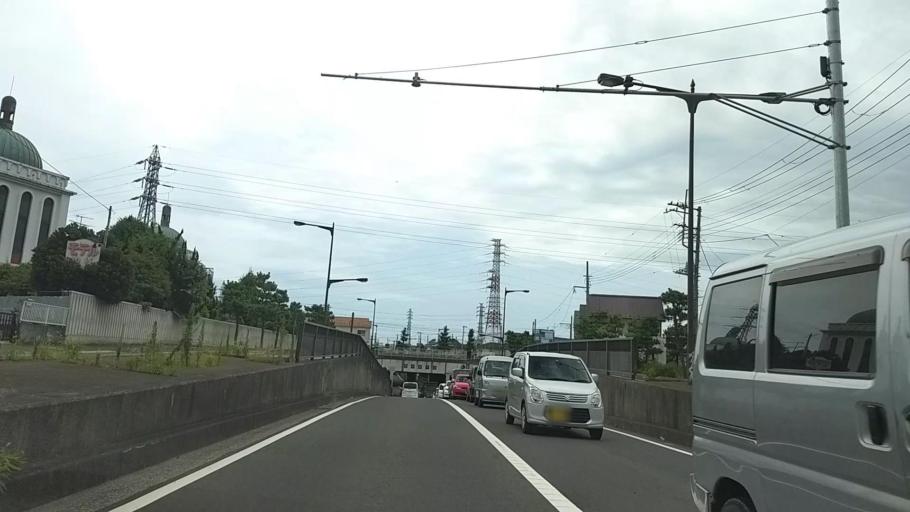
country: JP
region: Kanagawa
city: Chigasaki
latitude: 35.3709
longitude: 139.3826
